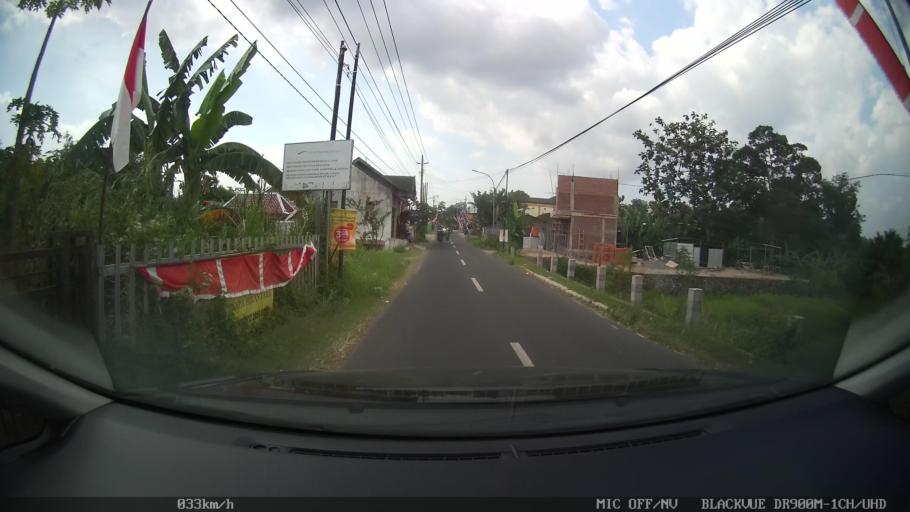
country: ID
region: Daerah Istimewa Yogyakarta
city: Gamping Lor
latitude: -7.8040
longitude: 110.3329
